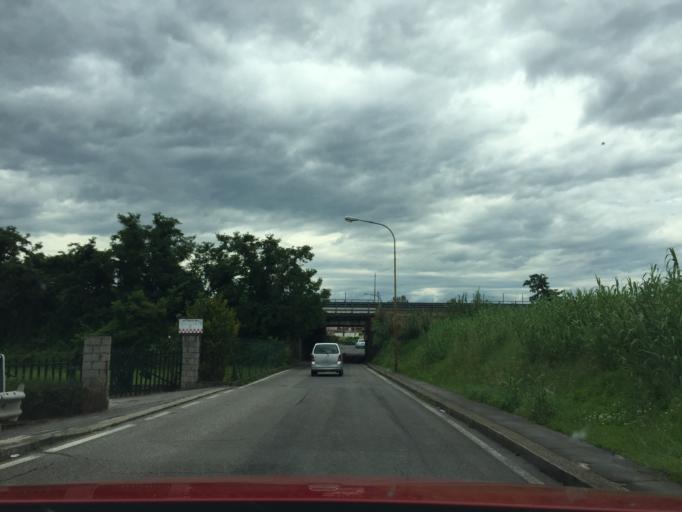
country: IT
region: Tuscany
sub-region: Provincia di Pistoia
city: Montecatini-Terme
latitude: 43.8751
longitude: 10.7769
